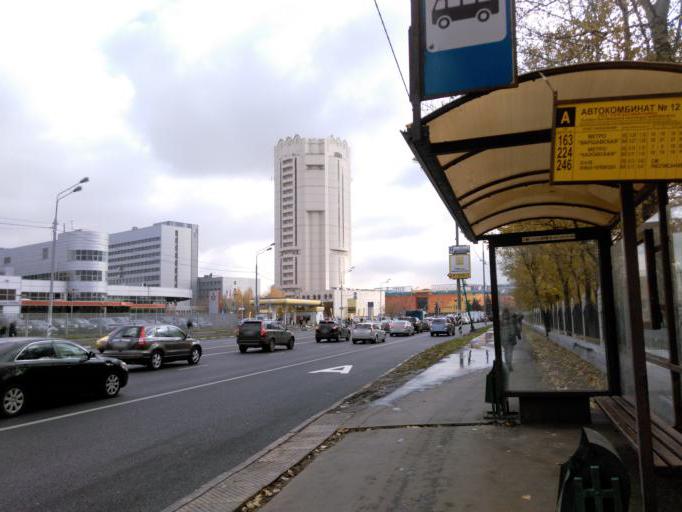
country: RU
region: Moskovskaya
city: Cheremushki
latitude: 55.6563
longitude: 37.5346
